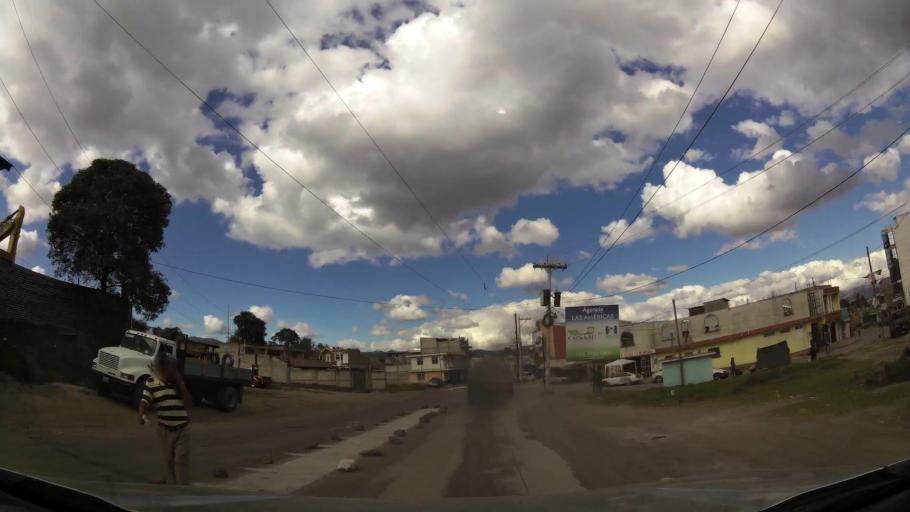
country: GT
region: Quetzaltenango
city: Quetzaltenango
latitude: 14.8288
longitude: -91.5367
